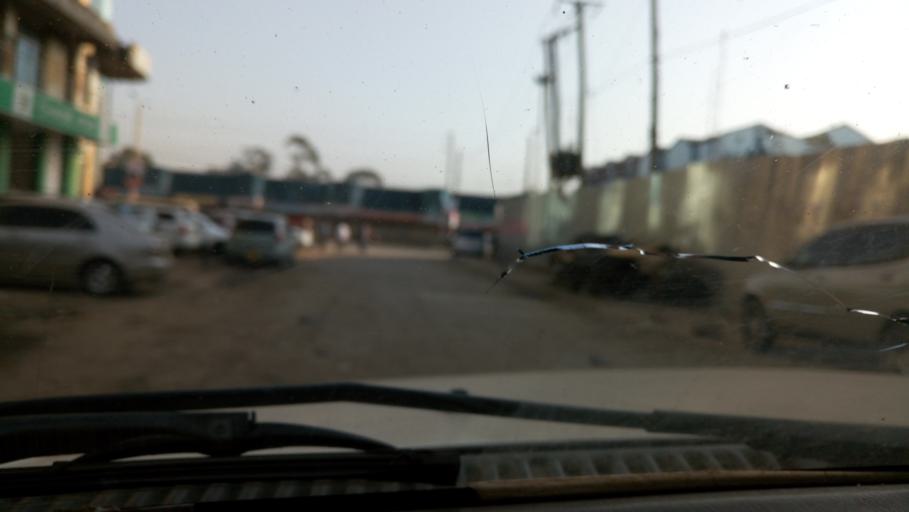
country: KE
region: Nairobi Area
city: Pumwani
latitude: -1.2799
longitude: 36.8494
